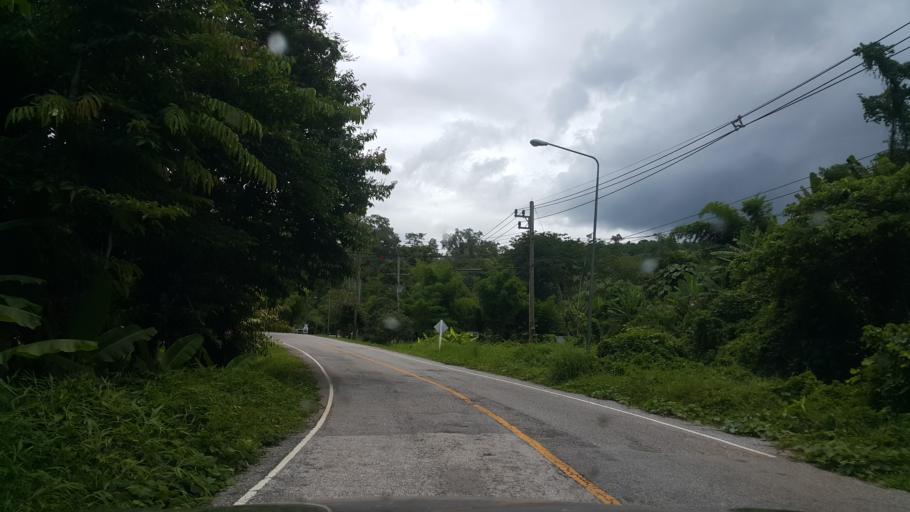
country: TH
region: Loei
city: Na Haeo
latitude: 17.6302
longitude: 100.8950
